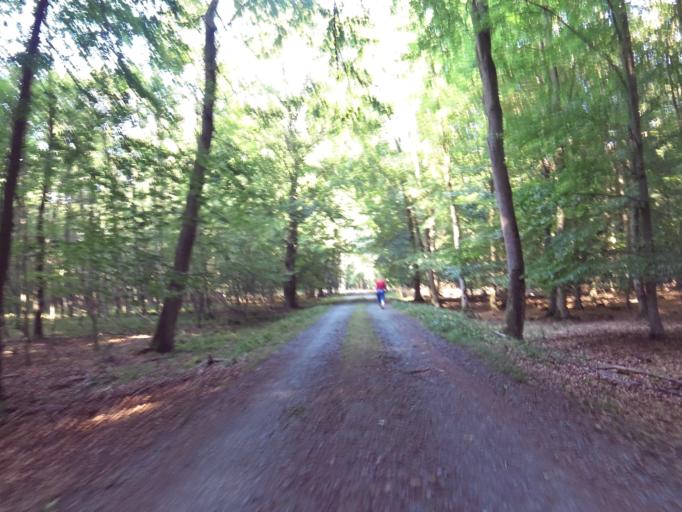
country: DE
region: Hesse
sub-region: Regierungsbezirk Darmstadt
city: Nauheim
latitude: 49.9850
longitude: 8.4979
